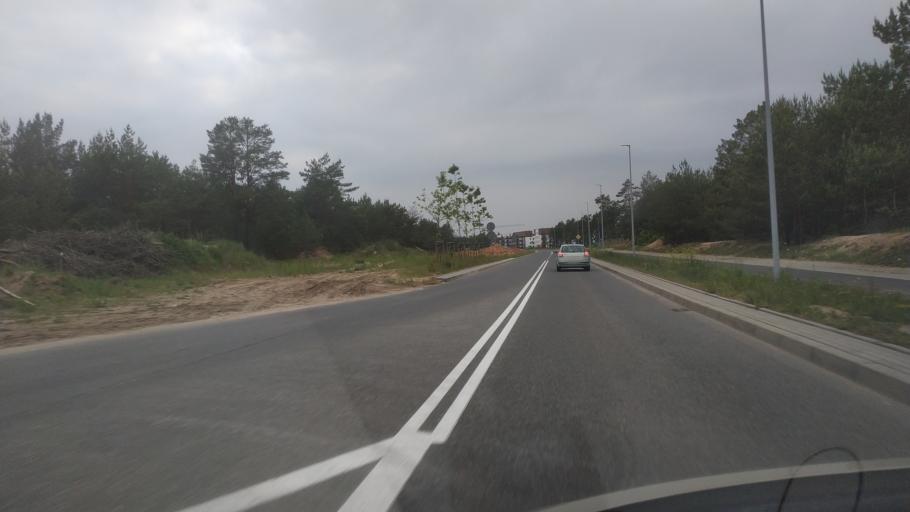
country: PL
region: Kujawsko-Pomorskie
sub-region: Powiat torunski
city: Lysomice
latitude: 53.0525
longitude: 18.6121
